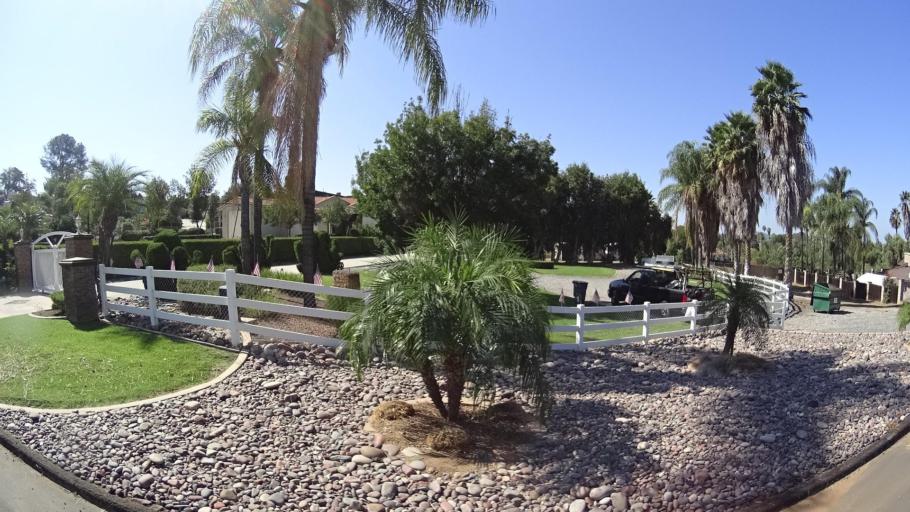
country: US
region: California
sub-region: San Diego County
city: Granite Hills
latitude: 32.7939
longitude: -116.9033
